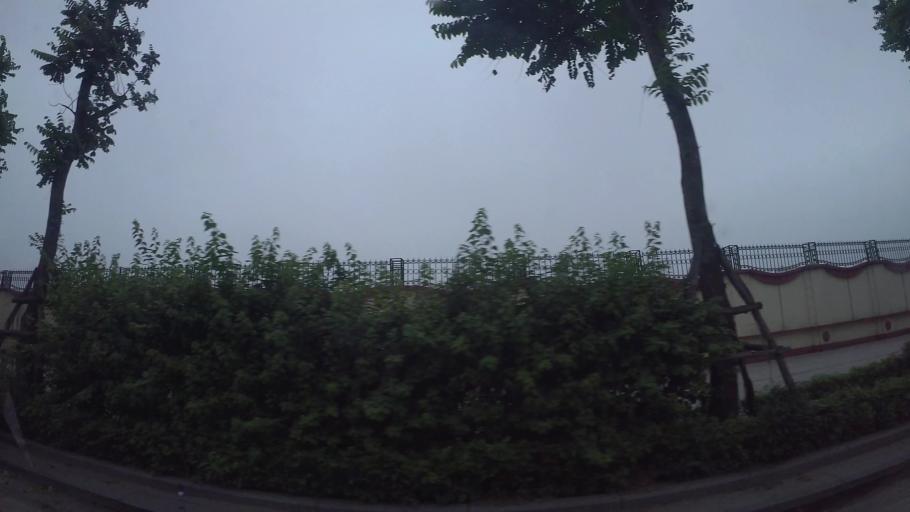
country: VN
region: Ha Noi
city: Dong Da
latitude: 20.9964
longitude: 105.8300
